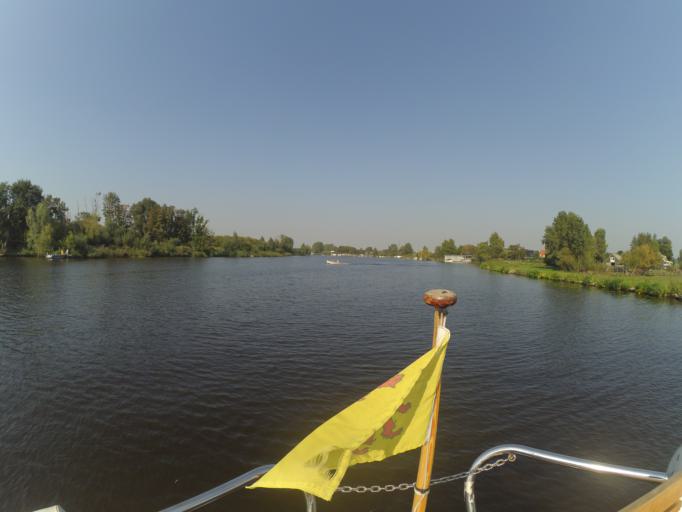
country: NL
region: North Holland
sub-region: Gemeente Heemstede
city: Heemstede
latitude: 52.3408
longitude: 4.6399
